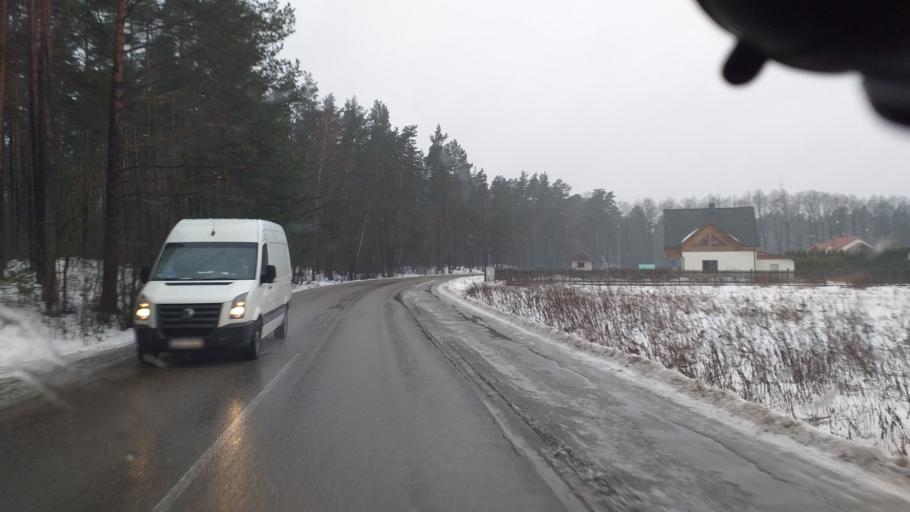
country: LV
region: Riga
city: Daugavgriva
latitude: 56.9820
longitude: 23.9934
